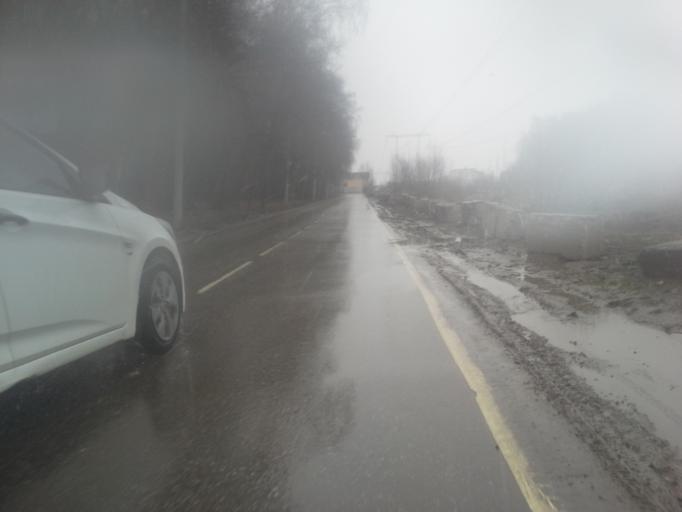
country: RU
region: Moskovskaya
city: Kommunarka
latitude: 55.5801
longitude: 37.4849
